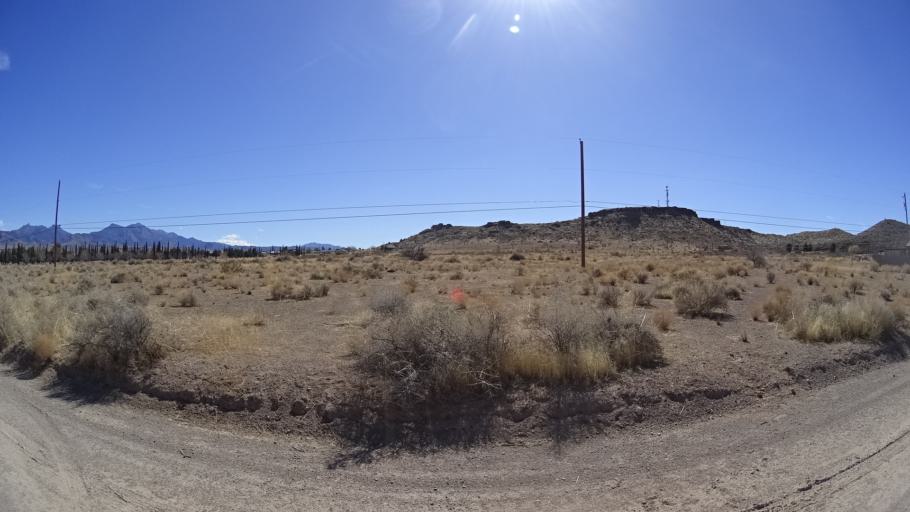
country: US
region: Arizona
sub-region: Mohave County
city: Kingman
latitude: 35.2039
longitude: -114.0375
